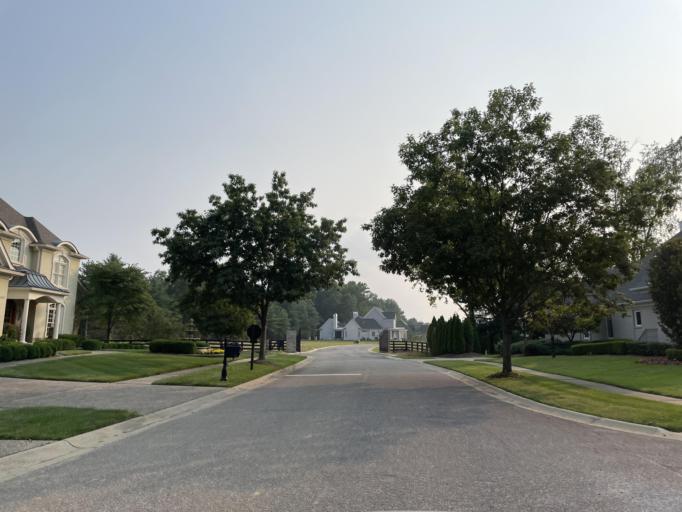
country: US
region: Kentucky
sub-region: Jefferson County
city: Prospect
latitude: 38.3574
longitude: -85.6208
